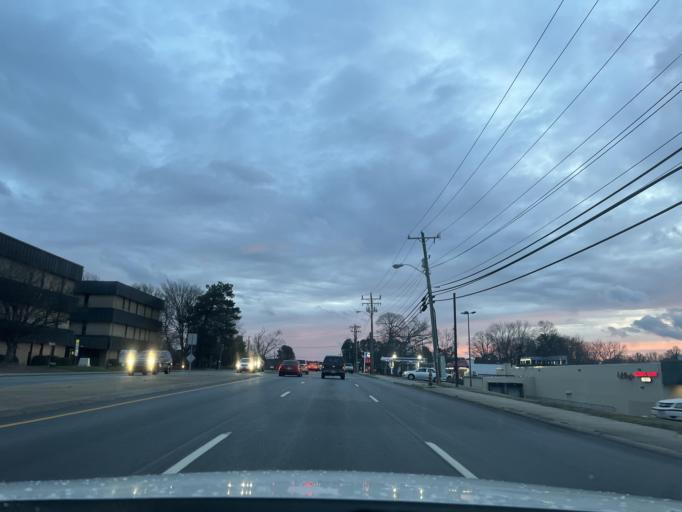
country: US
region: North Carolina
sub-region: Guilford County
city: Greensboro
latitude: 36.0386
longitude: -79.8499
